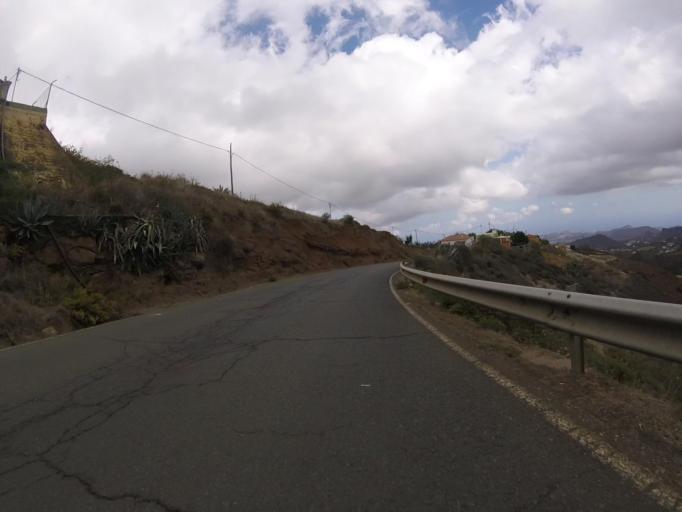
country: ES
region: Canary Islands
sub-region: Provincia de Las Palmas
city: Vega de San Mateo
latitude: 27.9982
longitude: -15.5670
